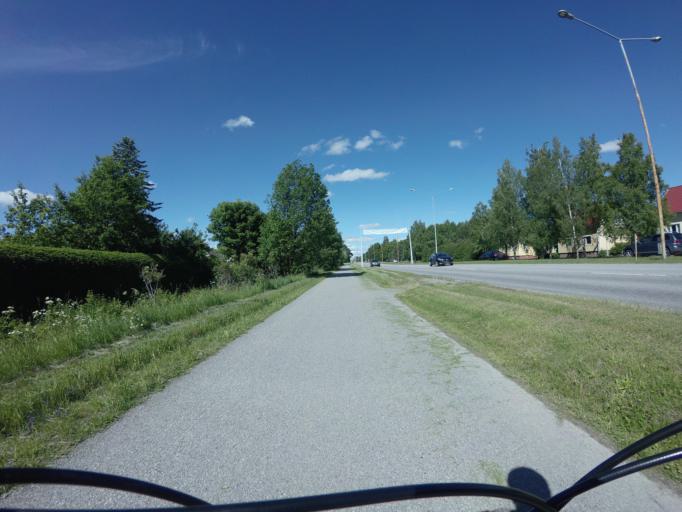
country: FI
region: Varsinais-Suomi
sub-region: Turku
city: Turku
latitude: 60.4796
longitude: 22.2697
